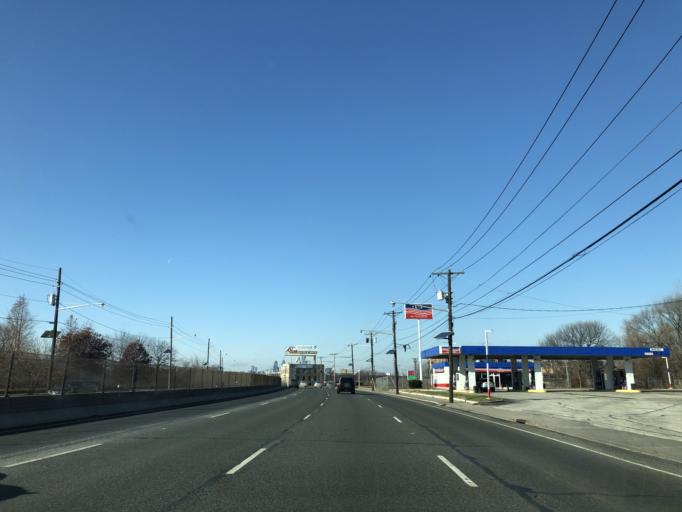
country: US
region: New Jersey
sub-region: Camden County
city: Wood-Lynne
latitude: 39.9402
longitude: -75.0959
